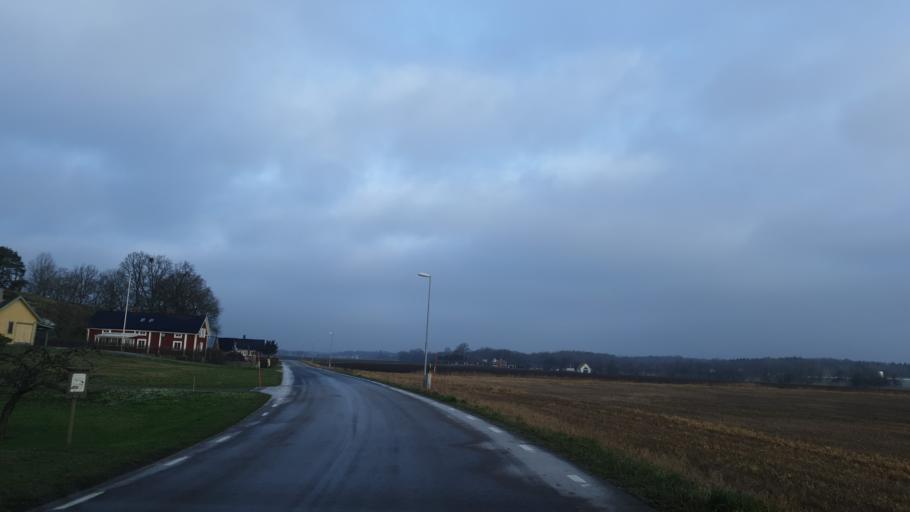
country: SE
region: Blekinge
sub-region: Karlshamns Kommun
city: Morrum
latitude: 56.1651
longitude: 14.7481
